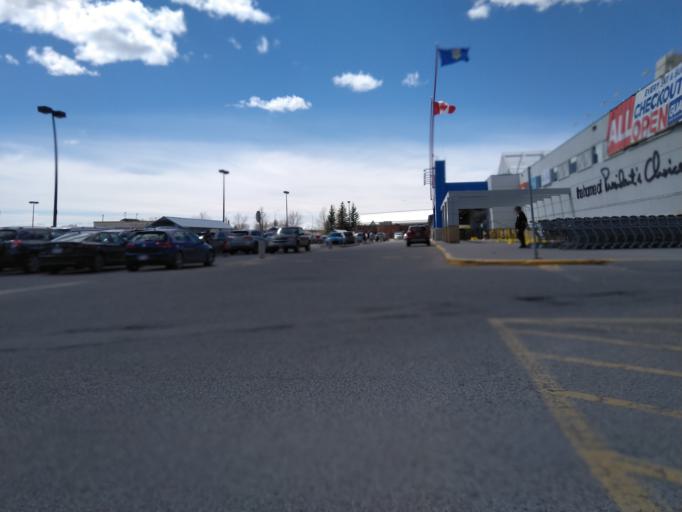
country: CA
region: Alberta
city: Calgary
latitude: 51.0193
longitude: -114.1730
